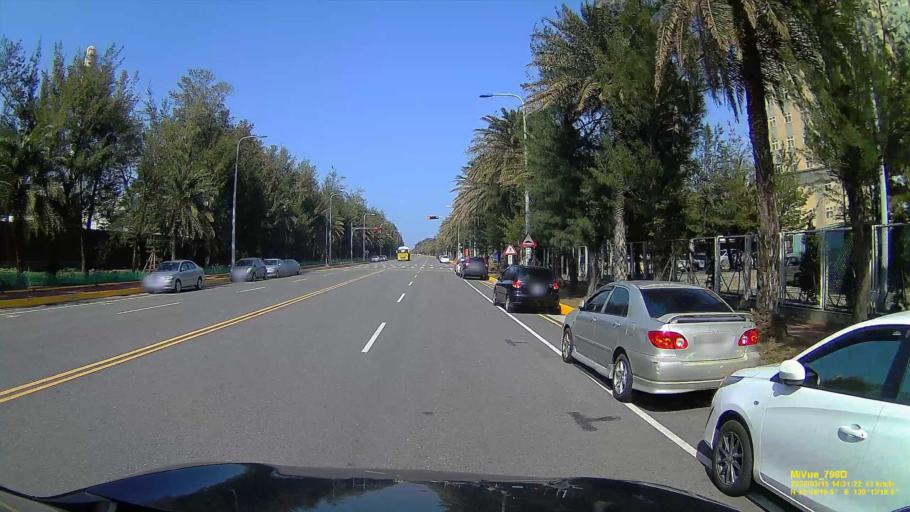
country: TW
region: Taiwan
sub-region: Yunlin
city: Douliu
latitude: 23.8044
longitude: 120.2212
